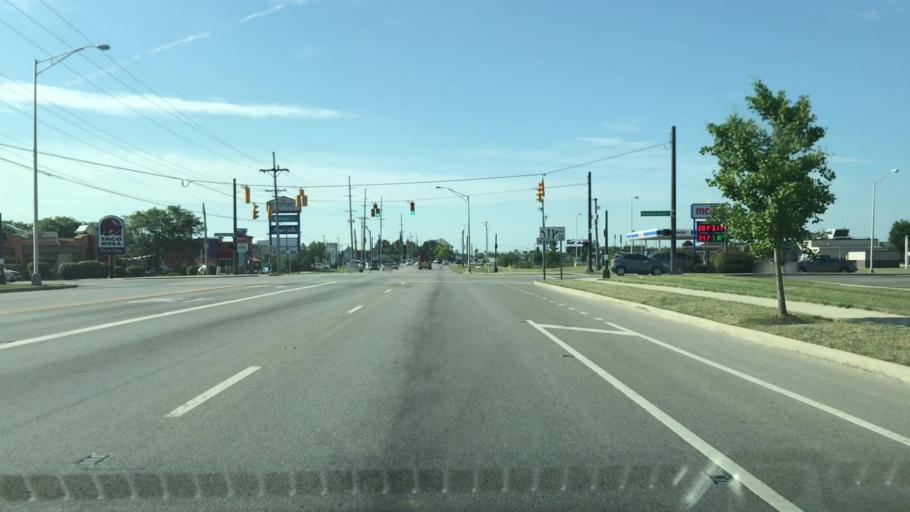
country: US
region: Ohio
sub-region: Franklin County
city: Lincoln Village
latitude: 39.9860
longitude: -83.1511
